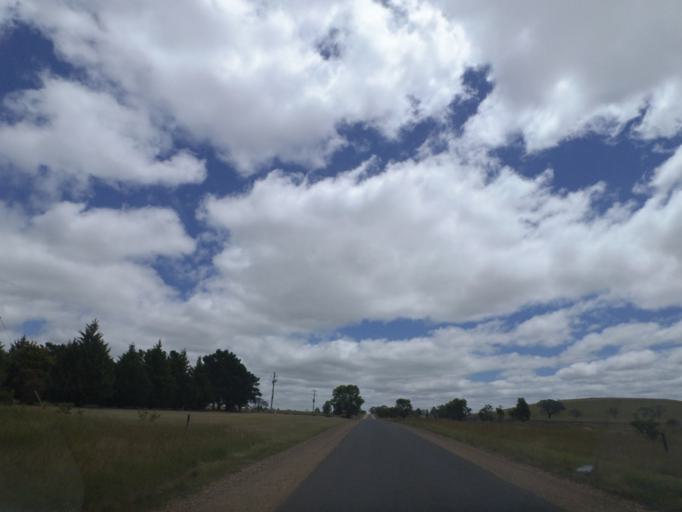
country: AU
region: Victoria
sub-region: Moorabool
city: Bacchus Marsh
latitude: -37.6188
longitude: 144.2537
